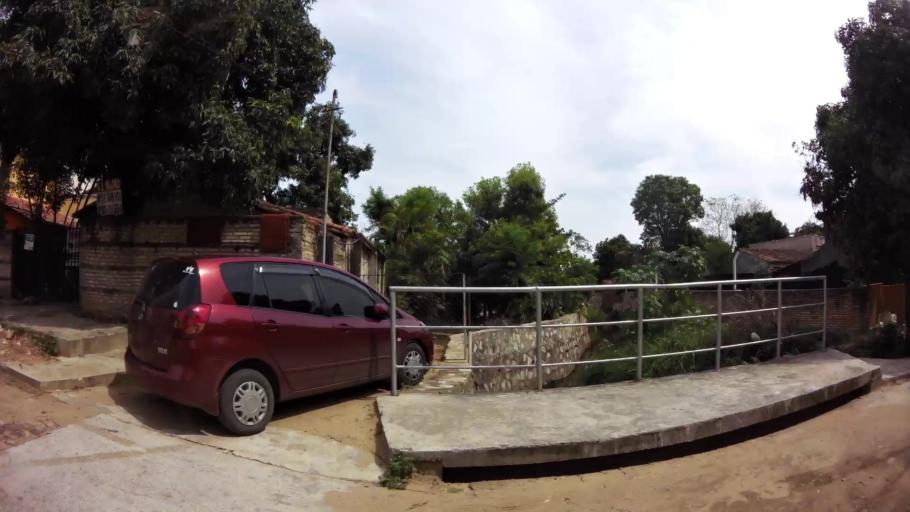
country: PY
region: Asuncion
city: Asuncion
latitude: -25.2614
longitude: -57.5854
